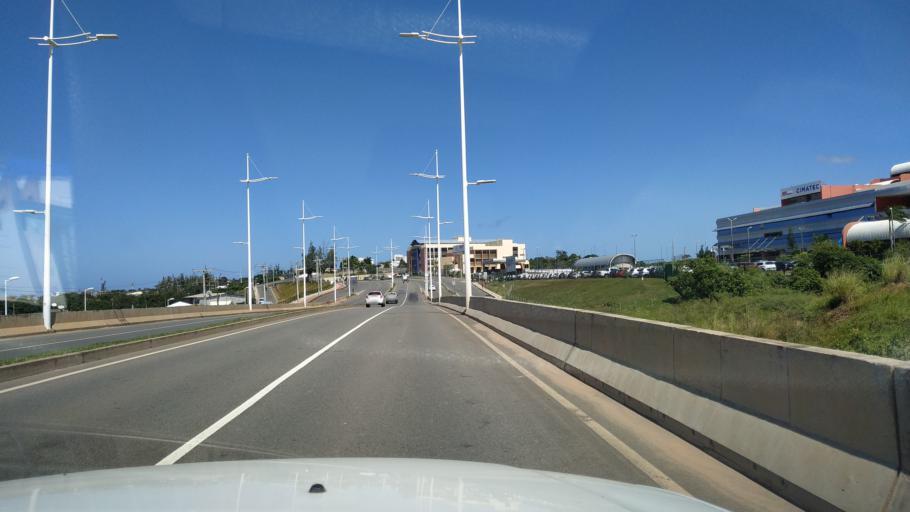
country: BR
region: Bahia
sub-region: Lauro De Freitas
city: Lauro de Freitas
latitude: -12.9374
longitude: -38.3857
